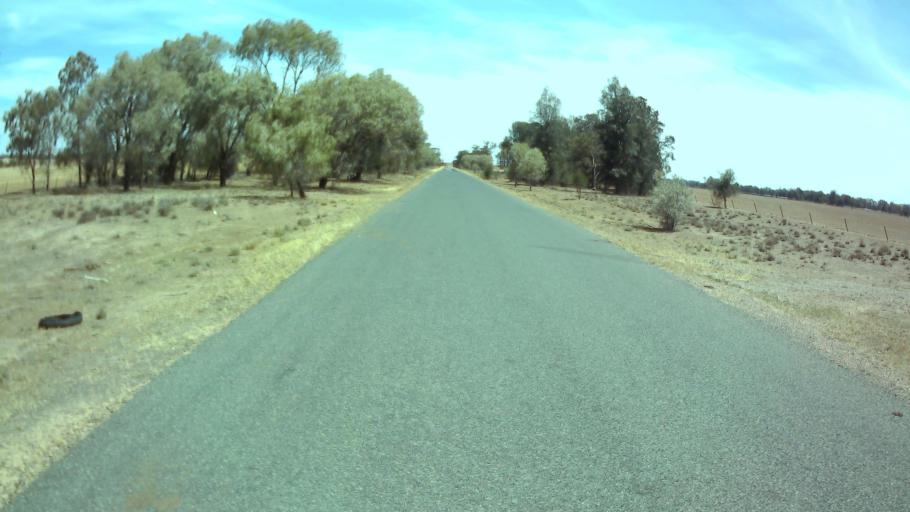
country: AU
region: New South Wales
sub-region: Weddin
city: Grenfell
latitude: -33.8764
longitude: 147.7437
